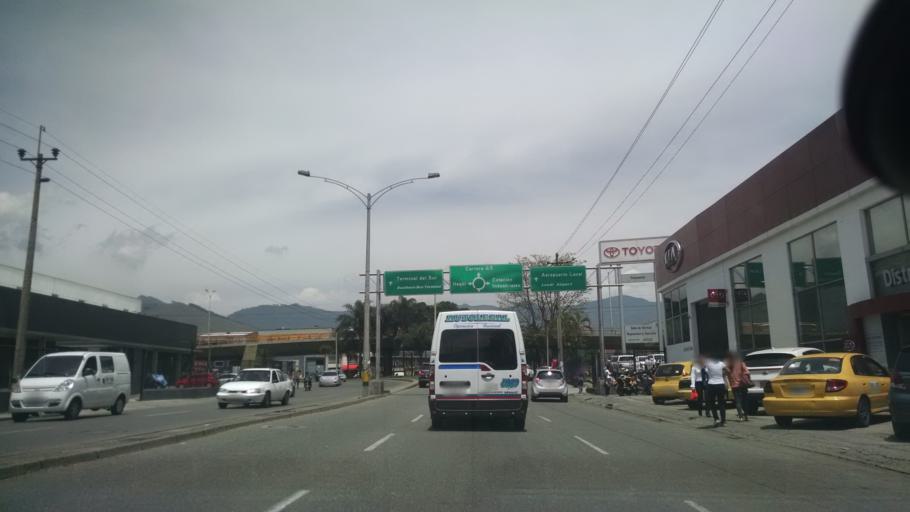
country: CO
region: Antioquia
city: Itagui
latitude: 6.2145
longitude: -75.5806
